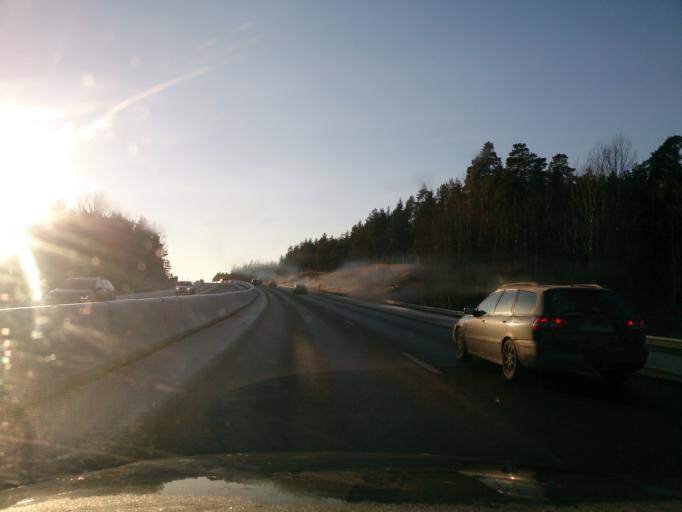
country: SE
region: OEstergoetland
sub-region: Norrkopings Kommun
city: Kimstad
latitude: 58.5460
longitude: 16.0455
